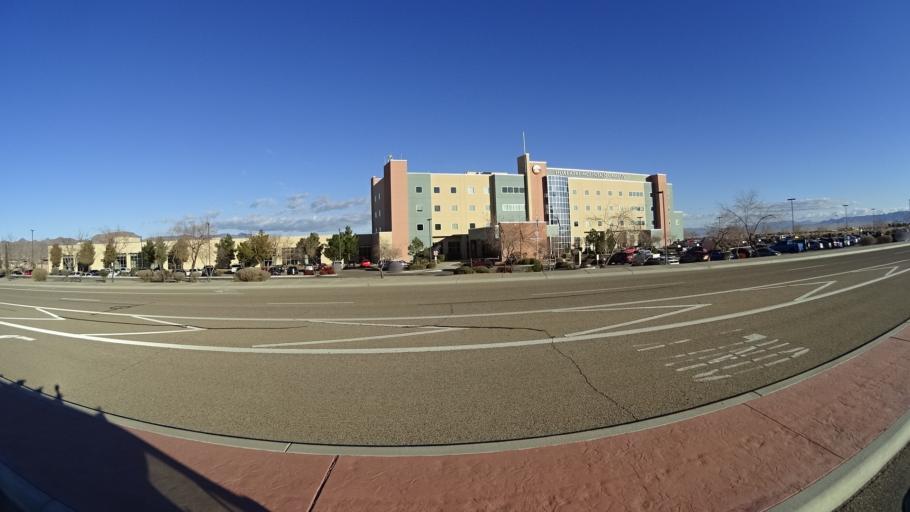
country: US
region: Arizona
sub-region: Mohave County
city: New Kingman-Butler
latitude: 35.2178
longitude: -113.9853
